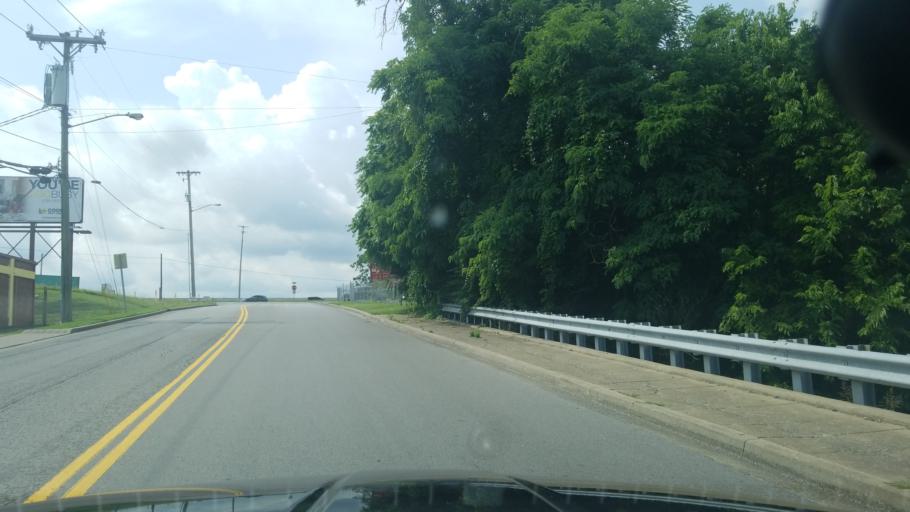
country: US
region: Tennessee
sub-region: Davidson County
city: Oak Hill
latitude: 36.0954
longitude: -86.7587
